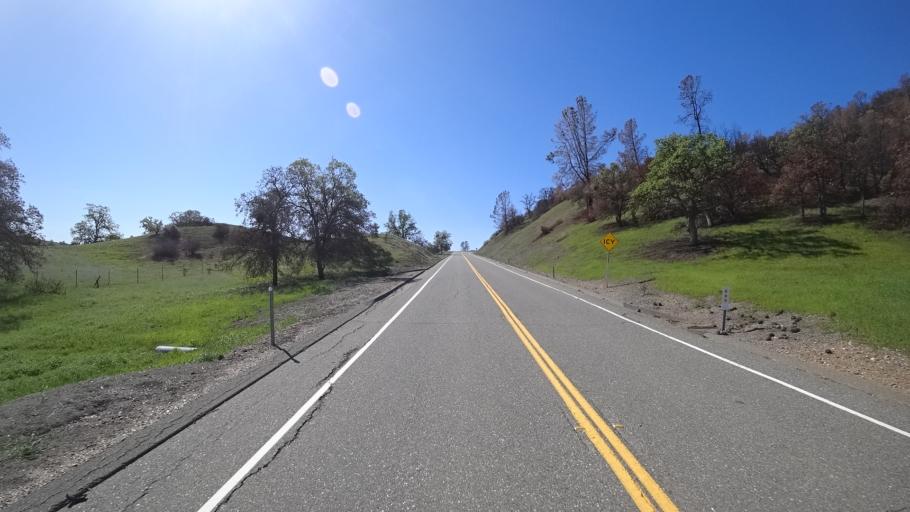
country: US
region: California
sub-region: Glenn County
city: Orland
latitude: 39.6550
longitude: -122.5938
